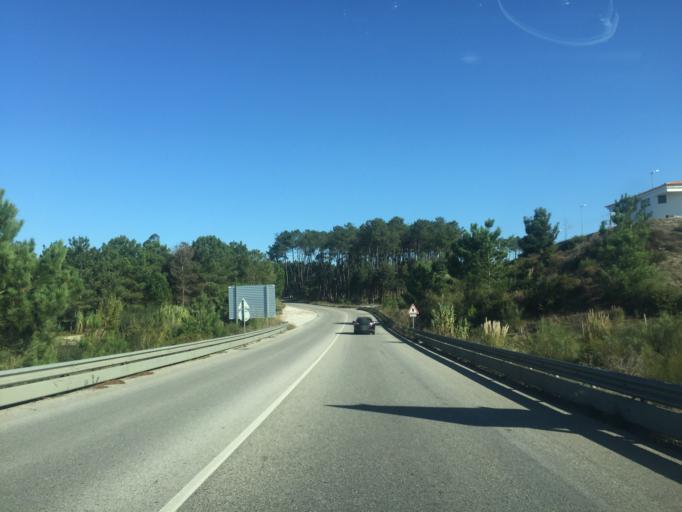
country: PT
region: Leiria
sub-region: Leiria
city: Amor
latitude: 39.8110
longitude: -8.8433
